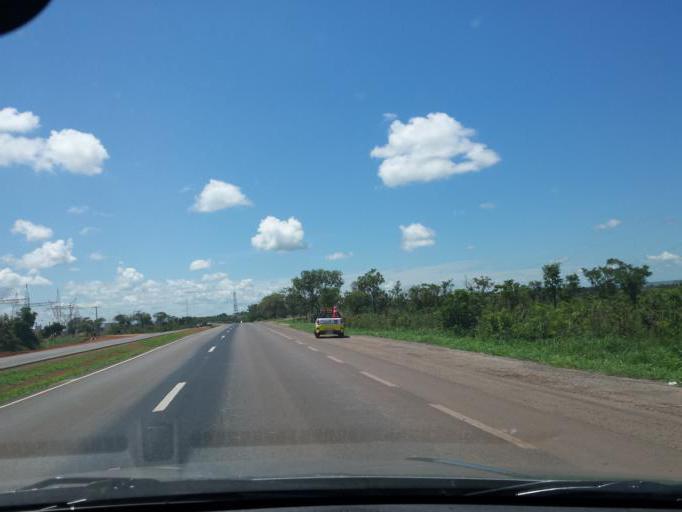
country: BR
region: Goias
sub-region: Luziania
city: Luziania
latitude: -16.3467
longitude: -47.8346
